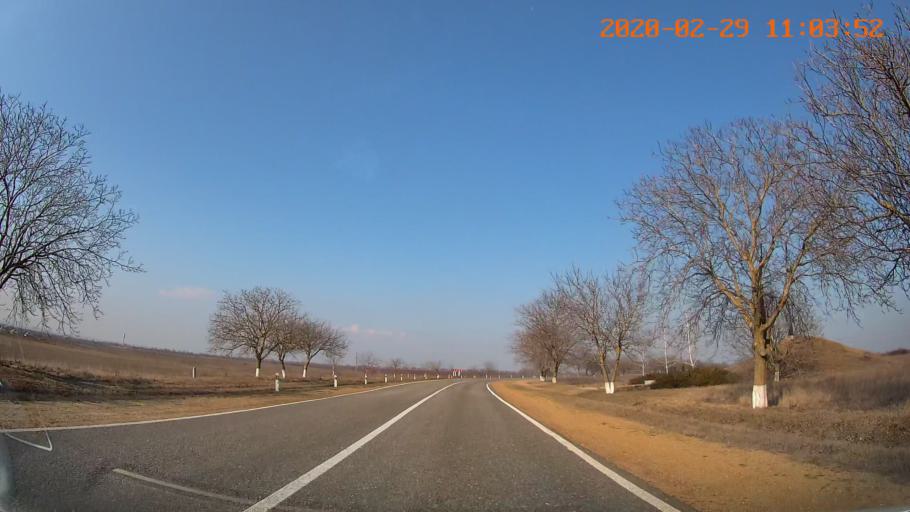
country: MD
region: Criuleni
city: Criuleni
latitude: 47.1823
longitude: 29.2095
